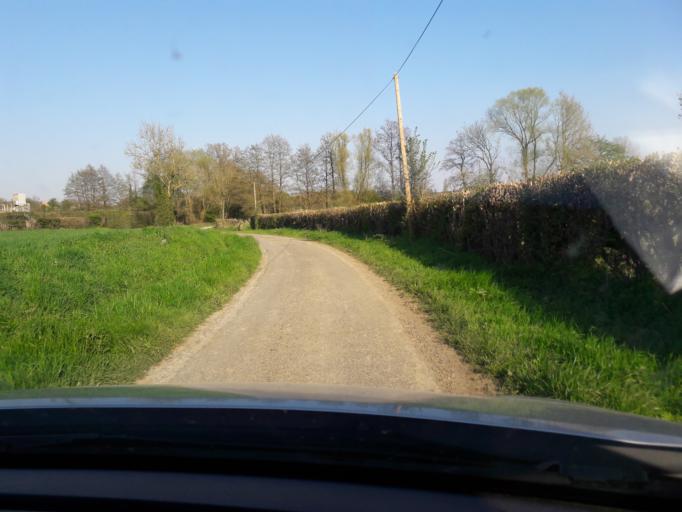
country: FR
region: Nord-Pas-de-Calais
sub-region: Departement du Nord
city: Sains-du-Nord
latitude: 50.1214
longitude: 4.0717
